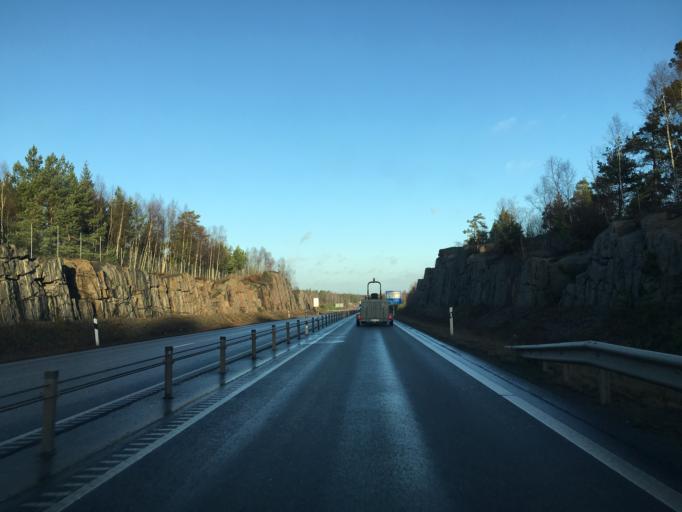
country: SE
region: Kalmar
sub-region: Vasterviks Kommun
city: Vaestervik
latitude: 57.7497
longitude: 16.5579
